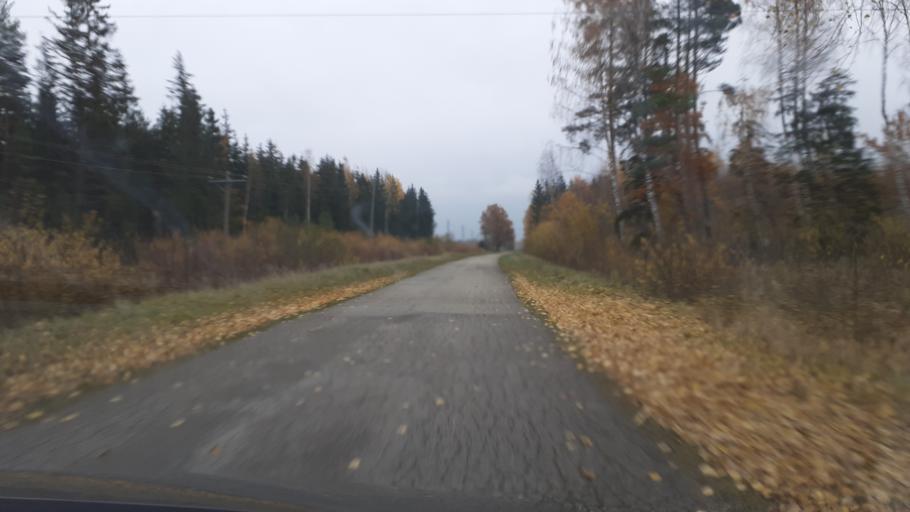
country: LV
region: Skrunda
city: Skrunda
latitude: 56.8565
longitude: 22.2425
